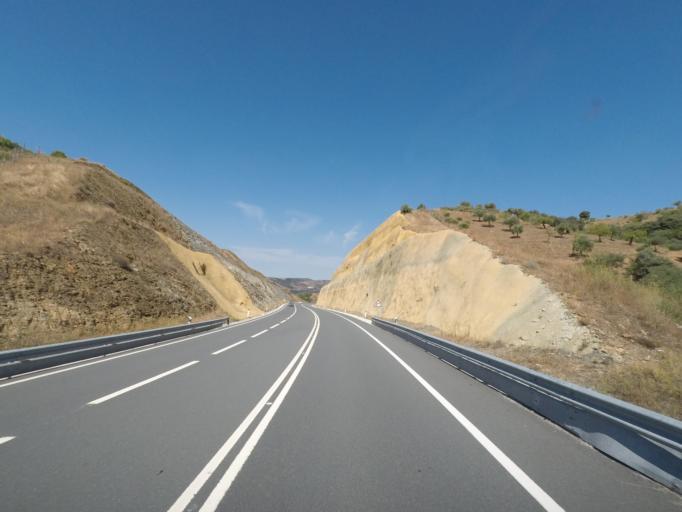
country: PT
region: Braganca
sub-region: Alfandega da Fe
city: Alfandega da Fe
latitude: 41.2955
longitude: -6.8968
